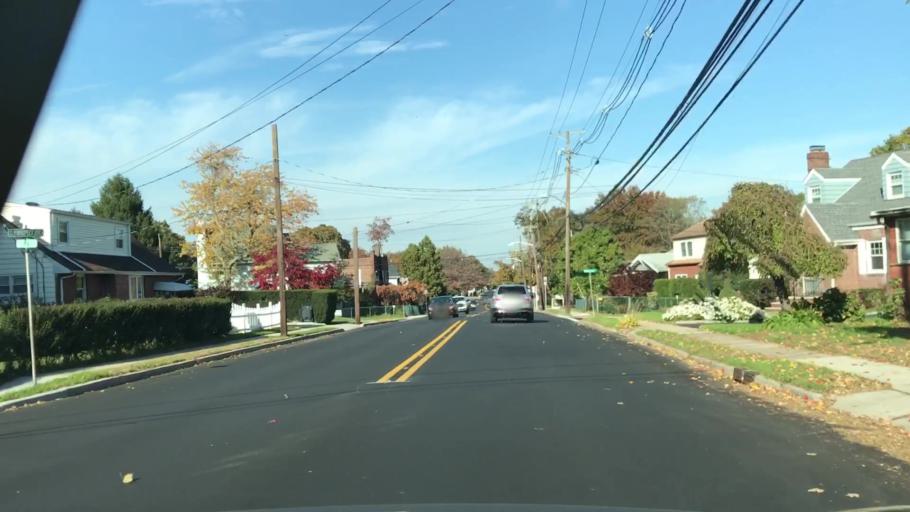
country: US
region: New Jersey
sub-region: Bergen County
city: Bergenfield
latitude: 40.9221
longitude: -74.0071
